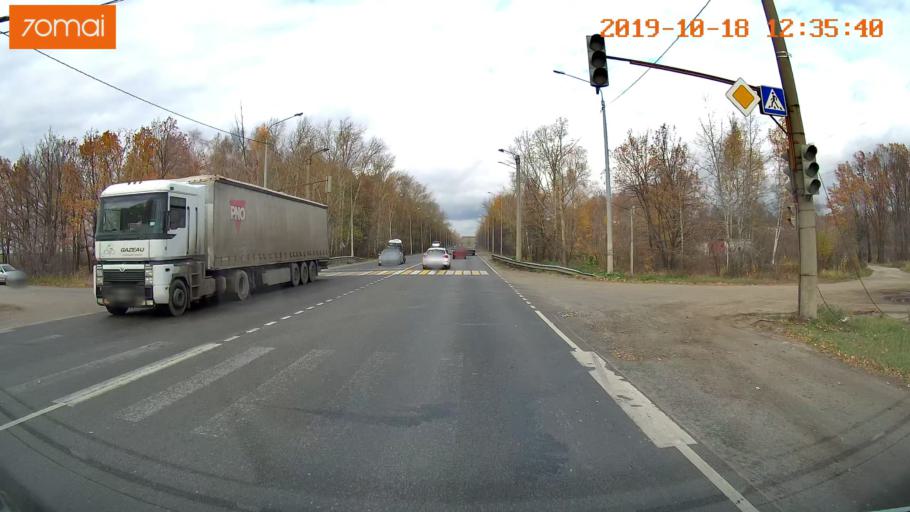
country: RU
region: Rjazan
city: Ryazan'
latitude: 54.6269
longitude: 39.6353
